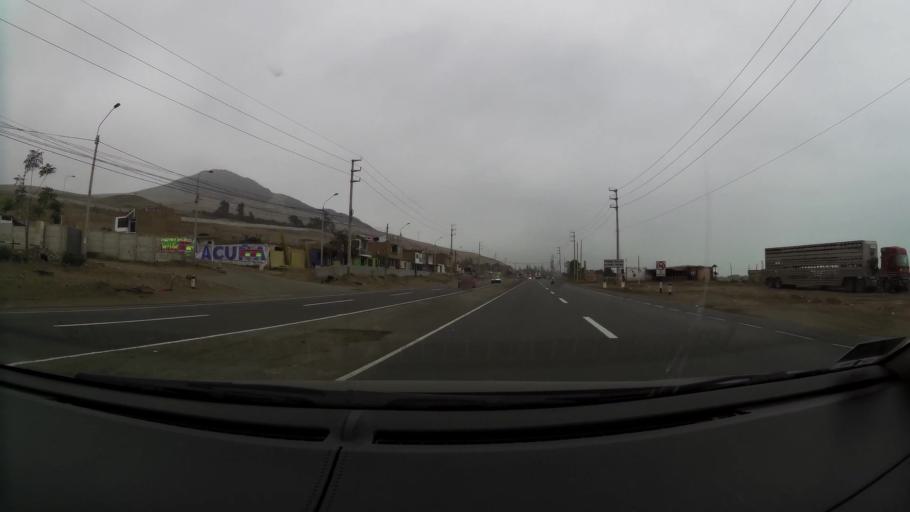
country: PE
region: Lima
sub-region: Provincia de Huaral
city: Chancay
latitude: -11.5981
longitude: -77.2517
